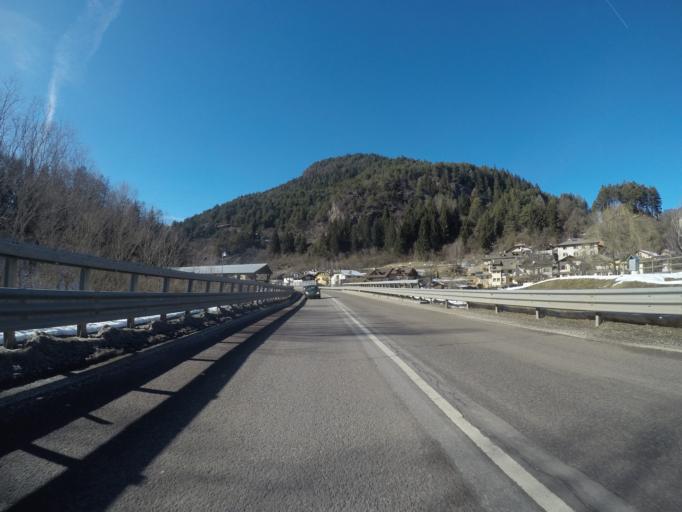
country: IT
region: Trentino-Alto Adige
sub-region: Provincia di Trento
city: Castello Molina di Fiemme
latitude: 46.2709
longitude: 11.4156
